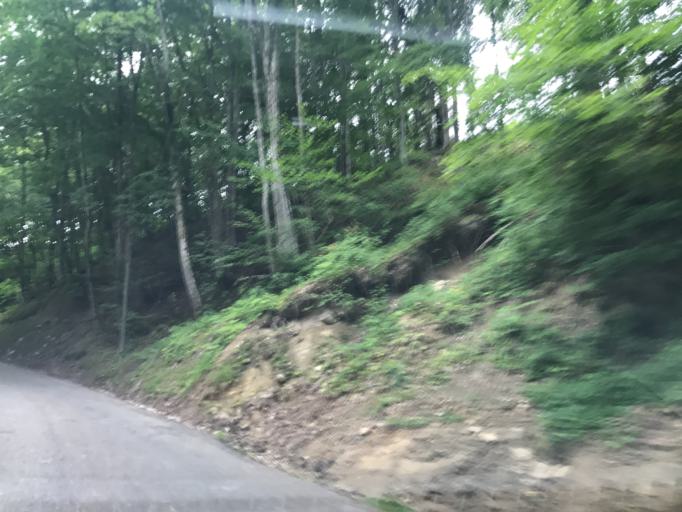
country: FR
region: Rhone-Alpes
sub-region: Departement de l'Isere
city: Saint-Vincent-de-Mercuze
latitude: 45.3867
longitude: 5.9313
